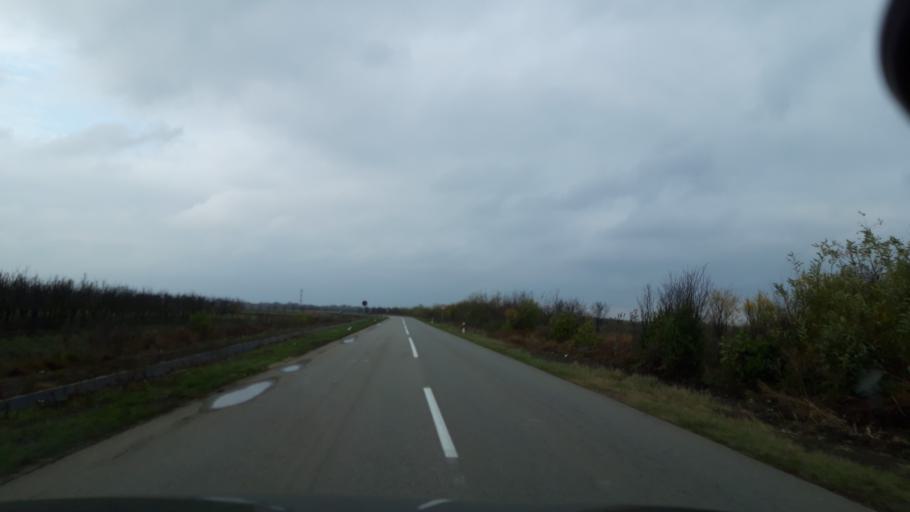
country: RS
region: Autonomna Pokrajina Vojvodina
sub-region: Severnobanatski Okrug
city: Novi Knezevac
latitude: 46.1107
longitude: 20.1027
